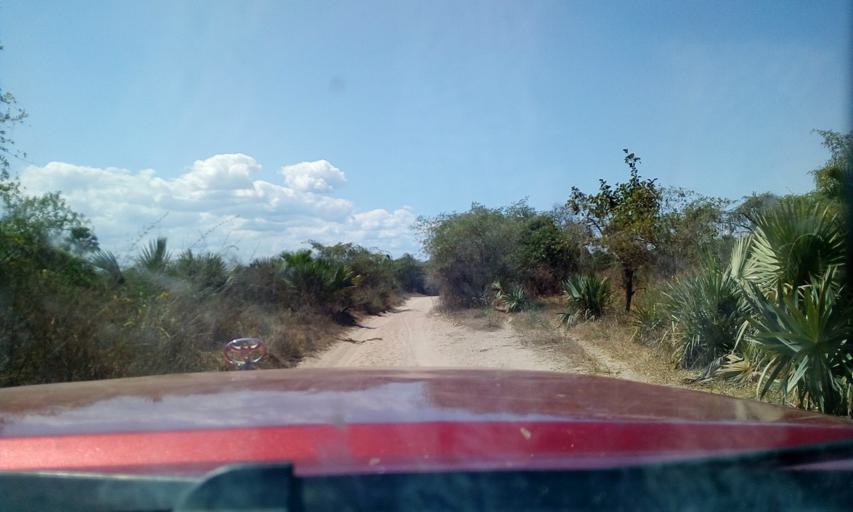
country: MG
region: Boeny
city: Sitampiky
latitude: -16.1269
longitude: 45.5062
